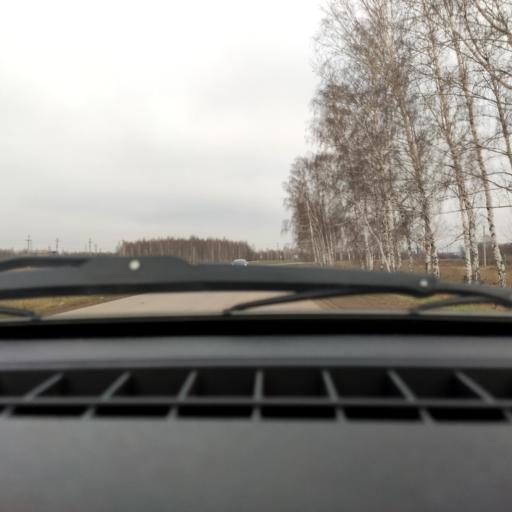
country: RU
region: Bashkortostan
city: Chishmy
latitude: 54.5750
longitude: 55.3545
